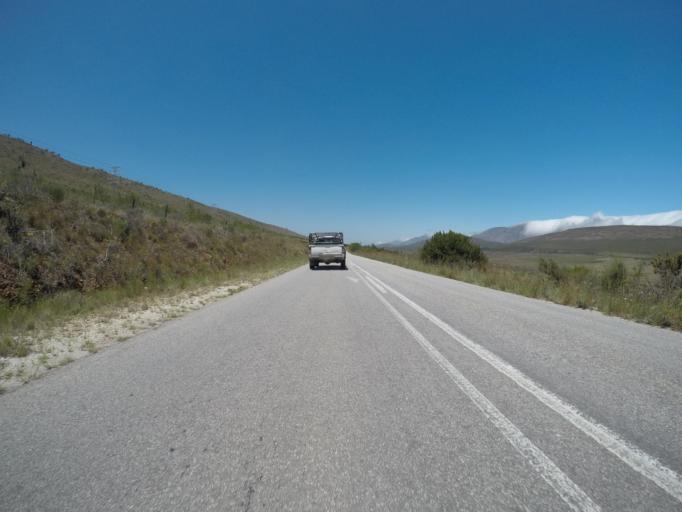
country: ZA
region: Eastern Cape
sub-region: Cacadu District Municipality
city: Kareedouw
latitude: -33.8401
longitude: 23.9310
